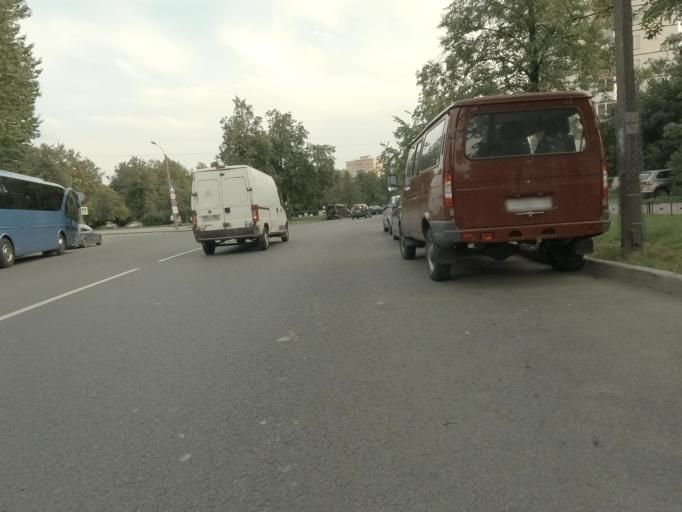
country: RU
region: St.-Petersburg
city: Dachnoye
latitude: 59.8460
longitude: 30.2677
